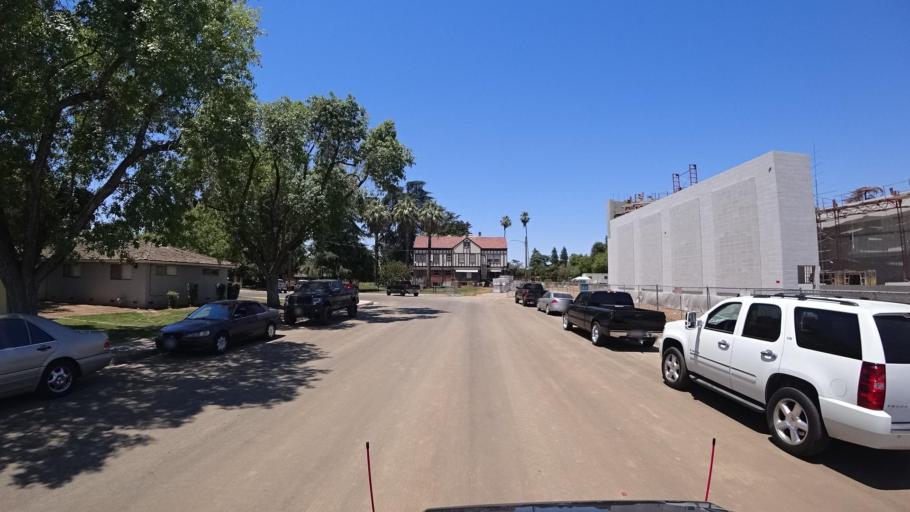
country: US
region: California
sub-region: Fresno County
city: Sunnyside
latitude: 36.7278
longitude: -119.7343
